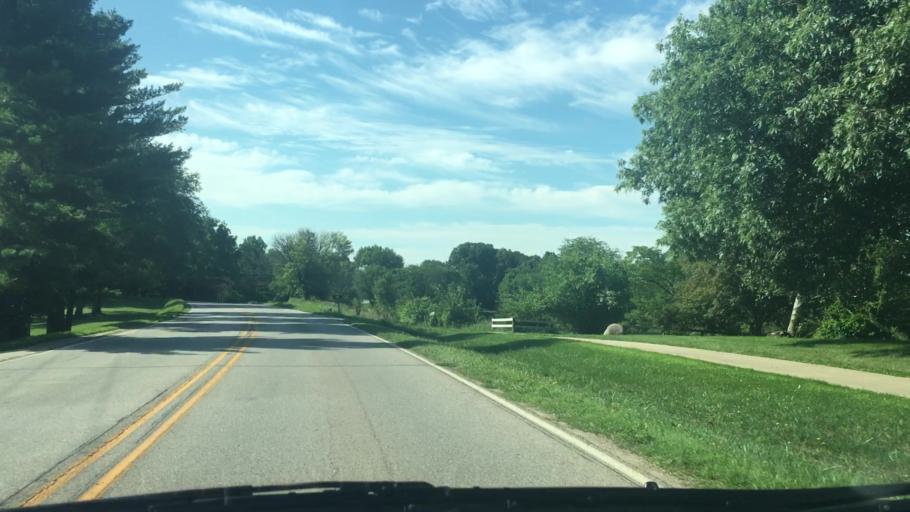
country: US
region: Iowa
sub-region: Johnson County
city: Coralville
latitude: 41.7108
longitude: -91.5508
